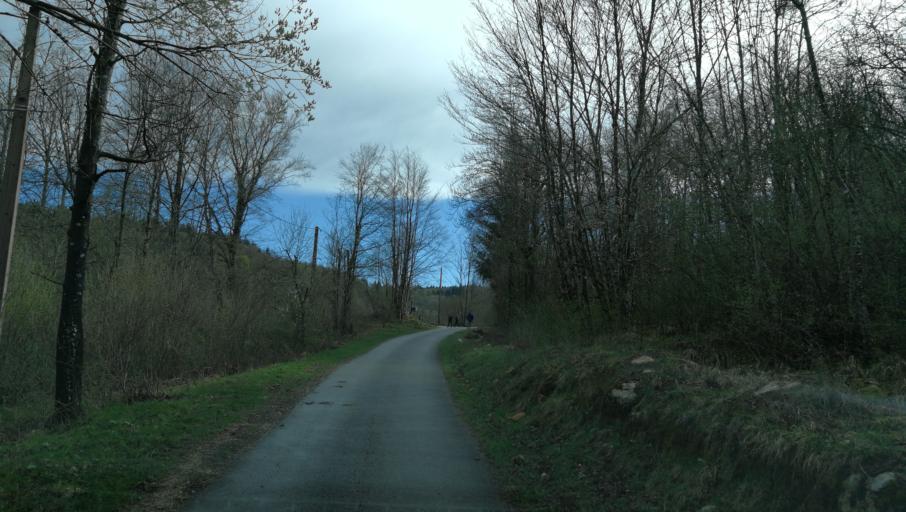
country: FR
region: Franche-Comte
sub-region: Departement du Jura
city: Lavans-les-Saint-Claude
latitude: 46.3139
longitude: 5.8111
